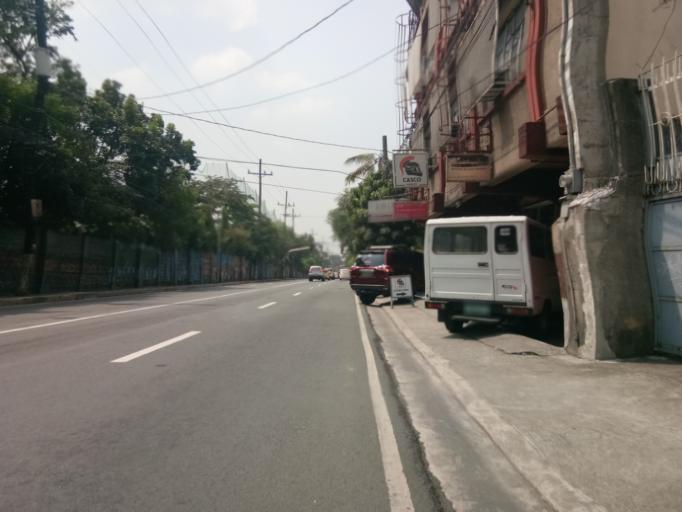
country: PH
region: Metro Manila
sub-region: Pasig
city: Pasig City
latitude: 14.6120
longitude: 121.0588
